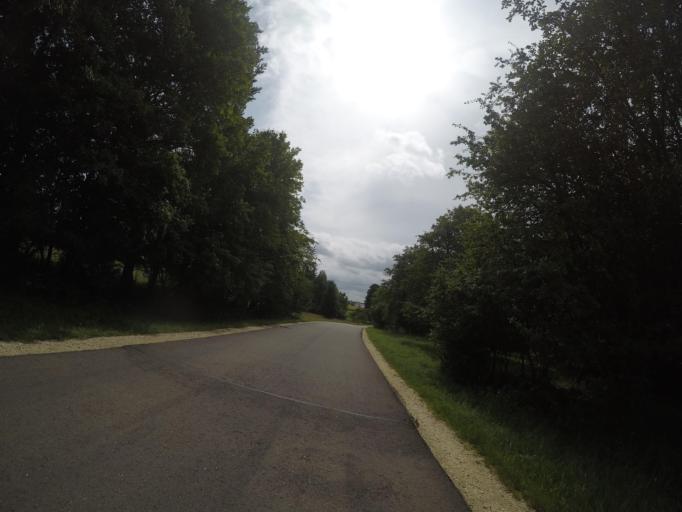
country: DE
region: Baden-Wuerttemberg
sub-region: Tuebingen Region
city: Berghulen
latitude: 48.4270
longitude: 9.7263
